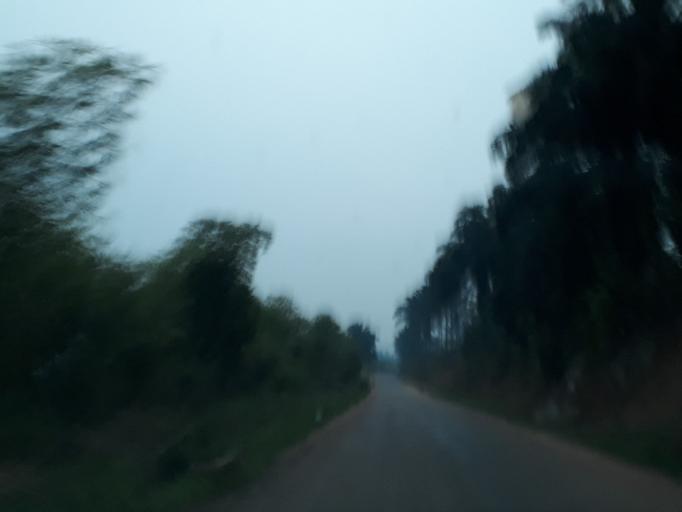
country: CD
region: Bandundu
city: Kikwit
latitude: -5.0775
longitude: 18.8816
